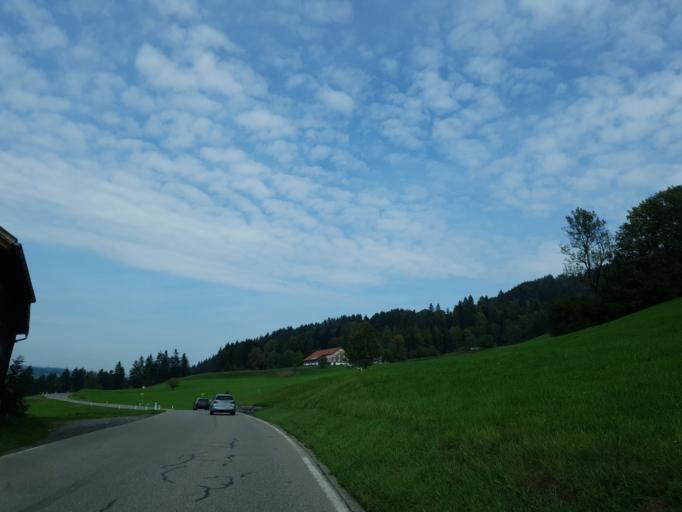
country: AT
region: Vorarlberg
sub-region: Politischer Bezirk Bregenz
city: Doren
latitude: 47.5066
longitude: 9.8656
